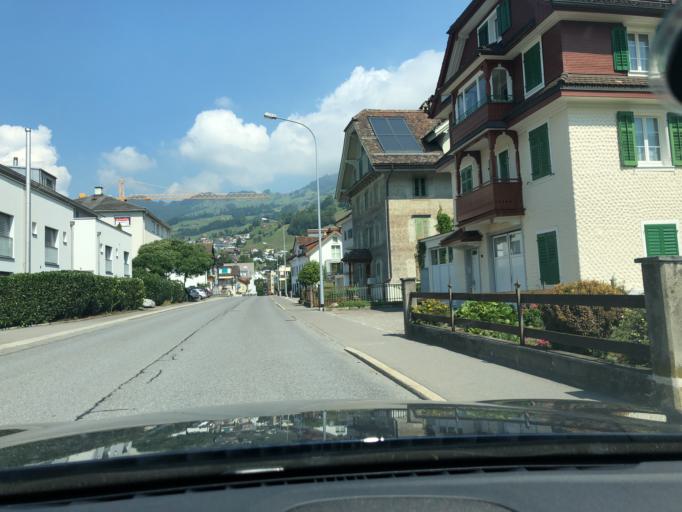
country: CH
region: Schwyz
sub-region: Bezirk Schwyz
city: Schwyz
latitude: 47.0167
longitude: 8.6579
